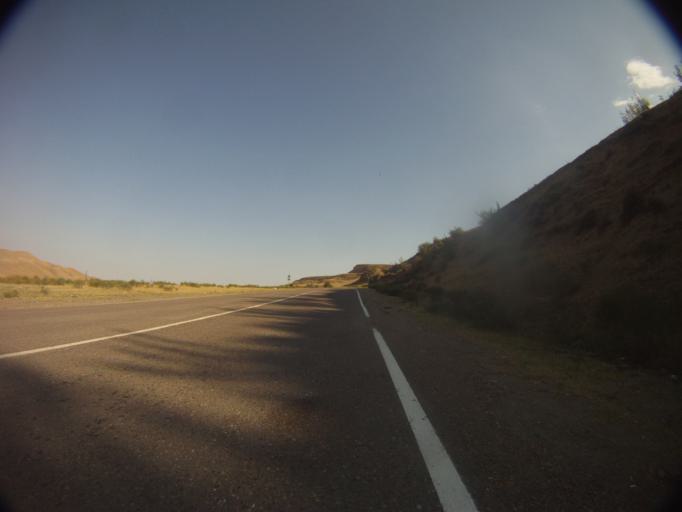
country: GE
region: Kvemo Kartli
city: Rust'avi
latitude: 41.5372
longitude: 44.9779
